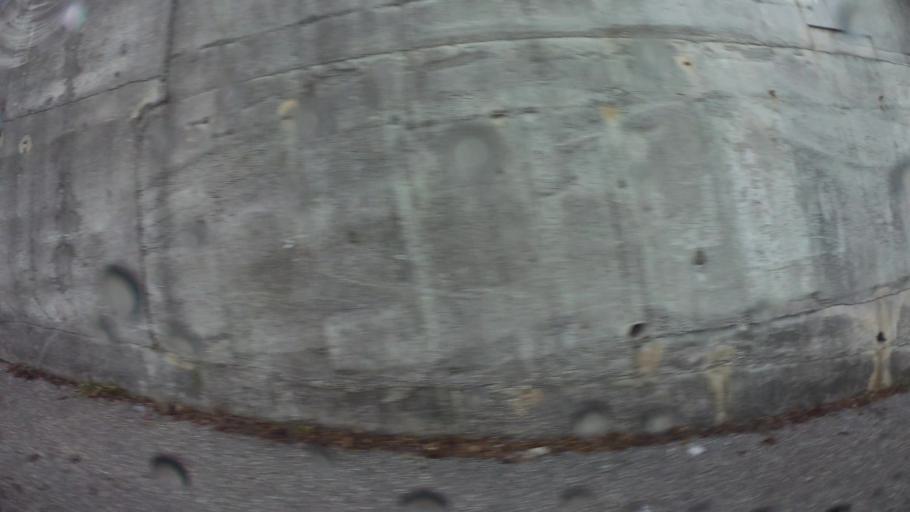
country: BA
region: Federation of Bosnia and Herzegovina
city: Cim
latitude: 43.3527
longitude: 17.7774
